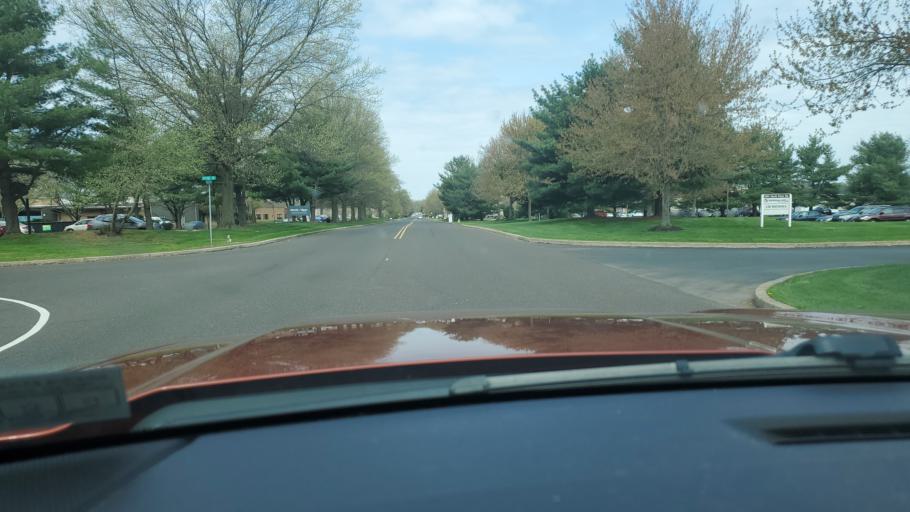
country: US
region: Pennsylvania
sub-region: Montgomery County
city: Hatfield
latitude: 40.2882
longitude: -75.2809
